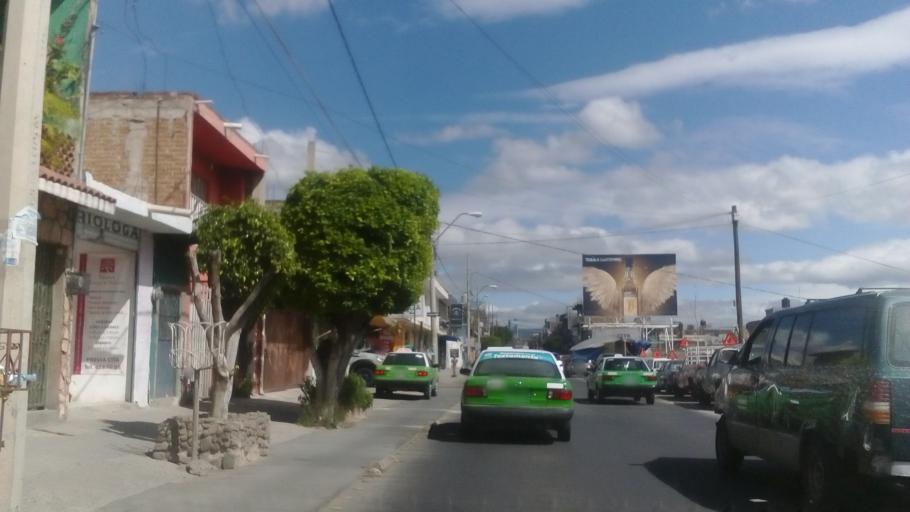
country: MX
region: Guanajuato
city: Leon
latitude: 21.1325
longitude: -101.7032
